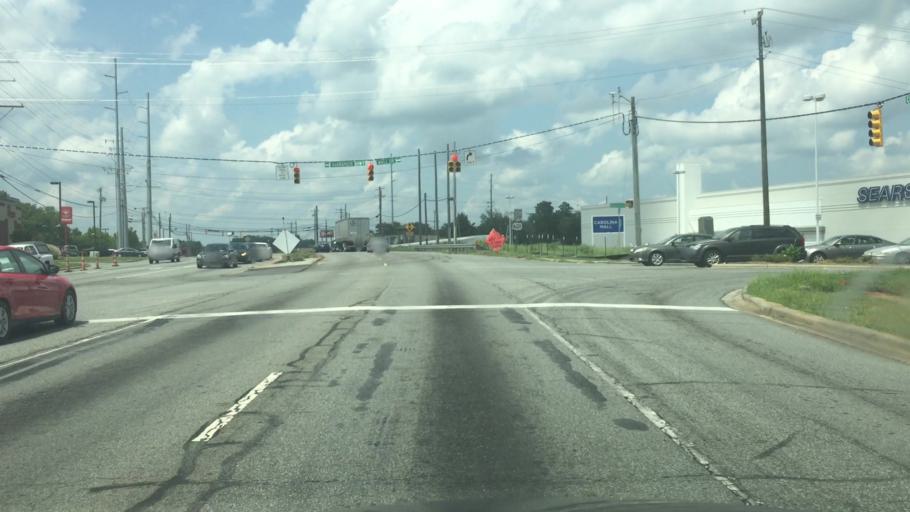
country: US
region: North Carolina
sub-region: Cabarrus County
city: Concord
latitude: 35.4376
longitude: -80.6048
